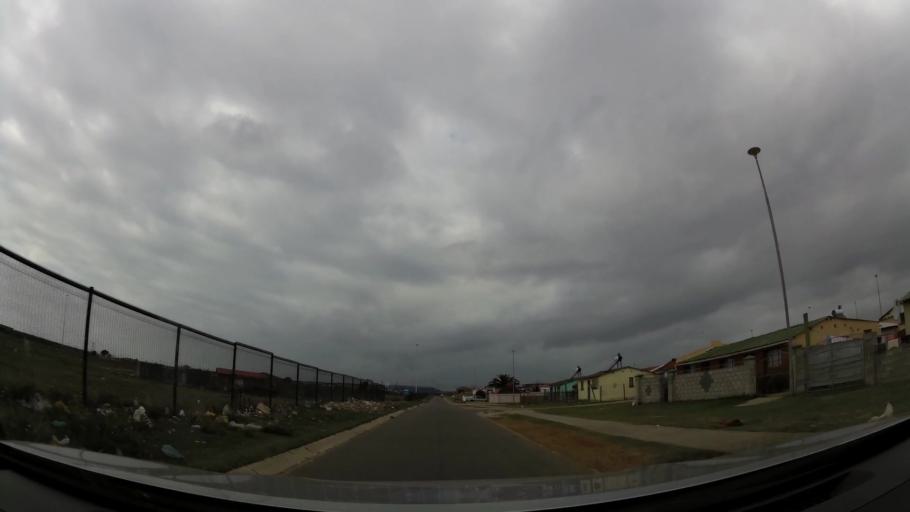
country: ZA
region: Eastern Cape
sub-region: Nelson Mandela Bay Metropolitan Municipality
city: Port Elizabeth
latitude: -33.8757
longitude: 25.5971
